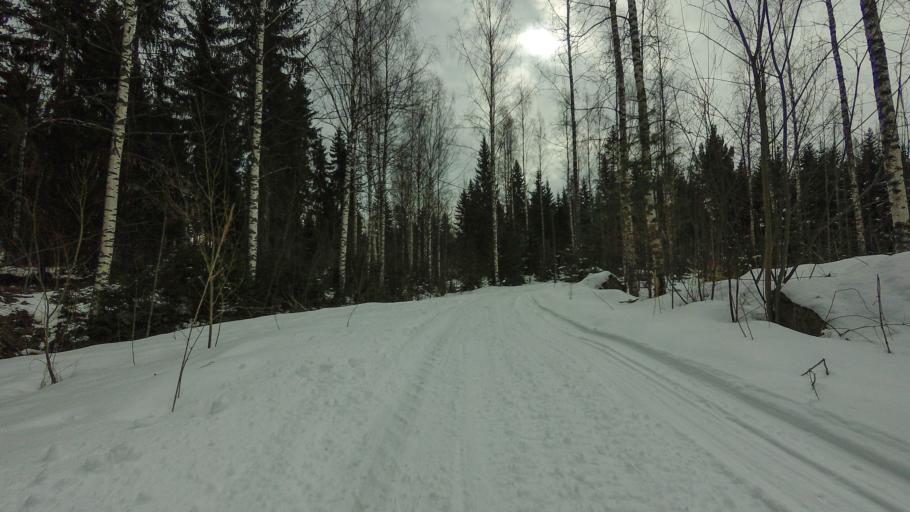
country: FI
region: Southern Savonia
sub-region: Savonlinna
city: Enonkoski
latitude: 62.1189
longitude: 28.6237
